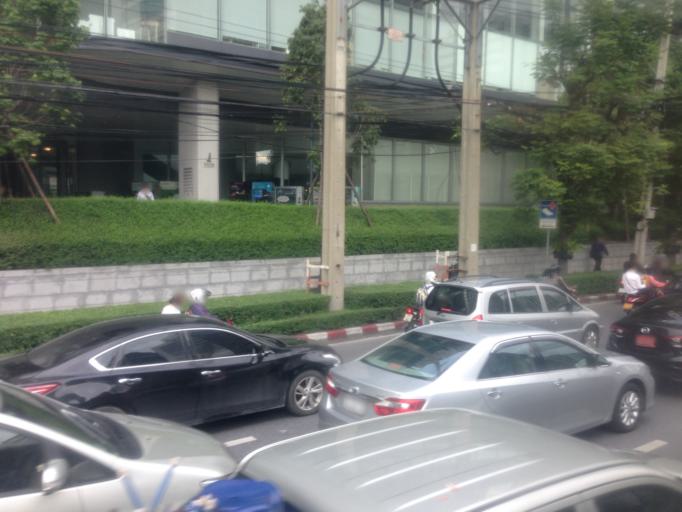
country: TH
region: Bangkok
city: Bang Rak
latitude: 13.7206
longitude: 100.5307
